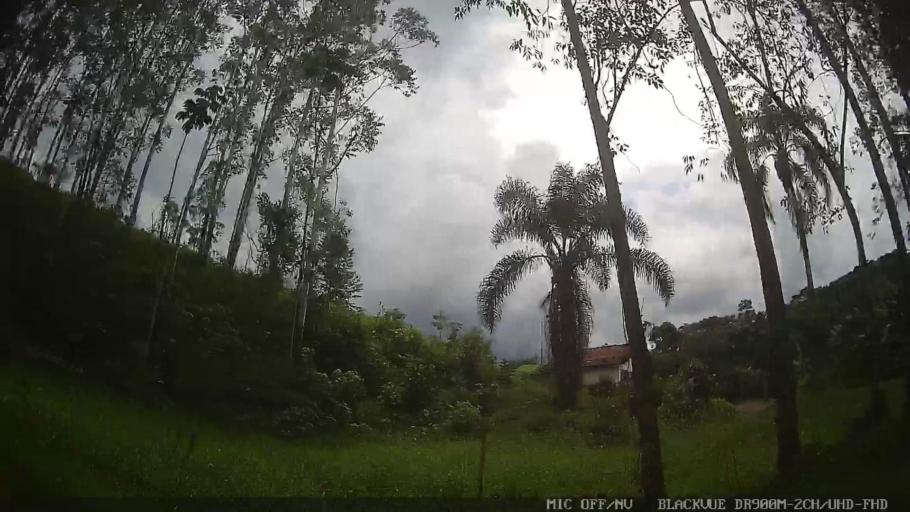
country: BR
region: Sao Paulo
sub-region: Santa Isabel
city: Santa Isabel
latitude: -23.3900
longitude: -46.2382
